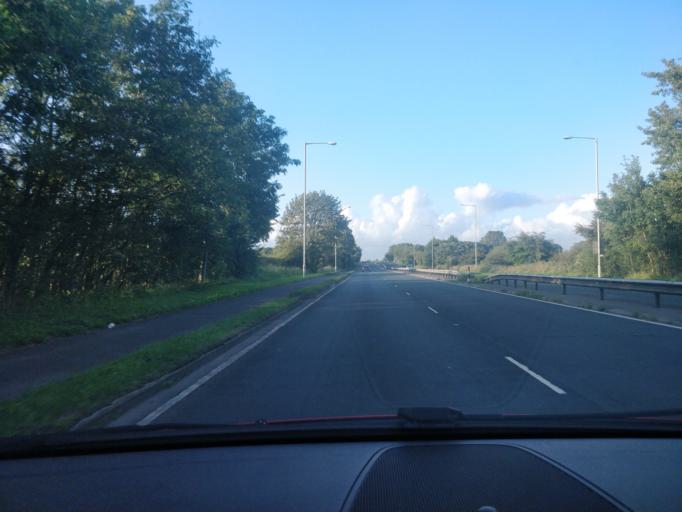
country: GB
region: England
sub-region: Lancashire
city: Croston
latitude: 53.7206
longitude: -2.7684
